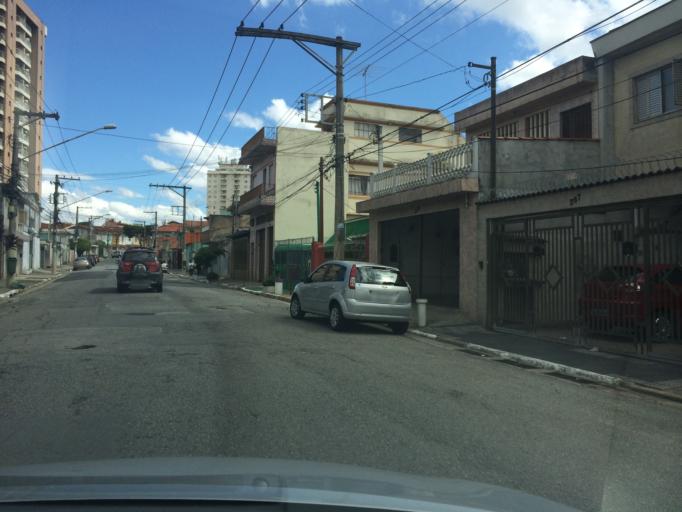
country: BR
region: Sao Paulo
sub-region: Guarulhos
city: Guarulhos
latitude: -23.5283
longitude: -46.5576
